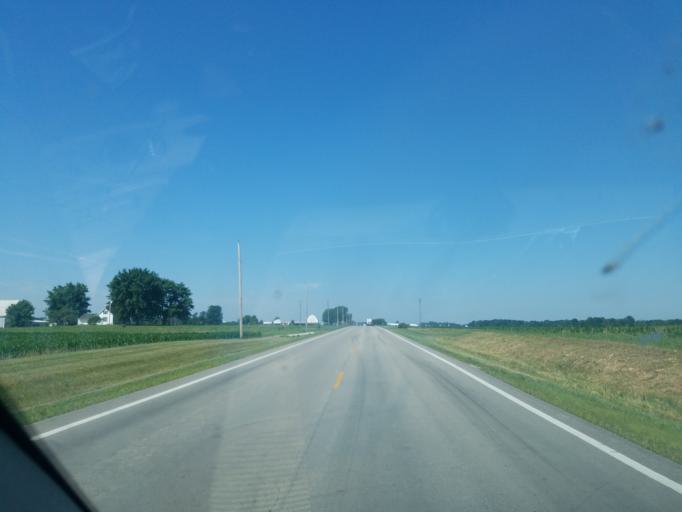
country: US
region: Ohio
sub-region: Shelby County
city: Botkins
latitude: 40.4387
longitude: -84.2277
